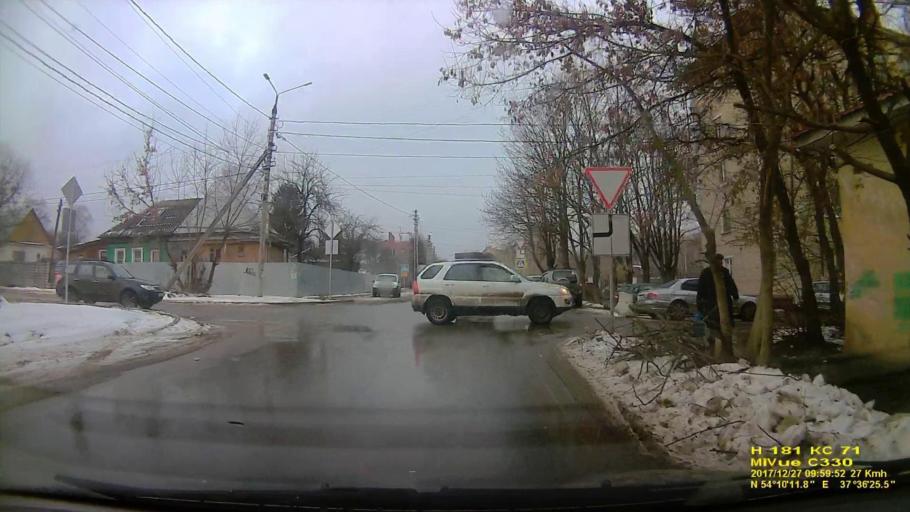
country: RU
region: Tula
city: Tula
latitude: 54.1701
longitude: 37.6066
